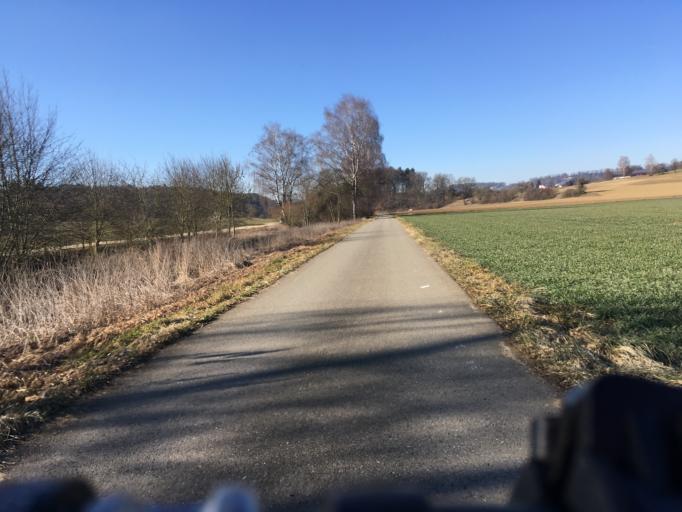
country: DE
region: Baden-Wuerttemberg
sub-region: Freiburg Region
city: Gailingen
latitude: 47.7275
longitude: 8.7457
